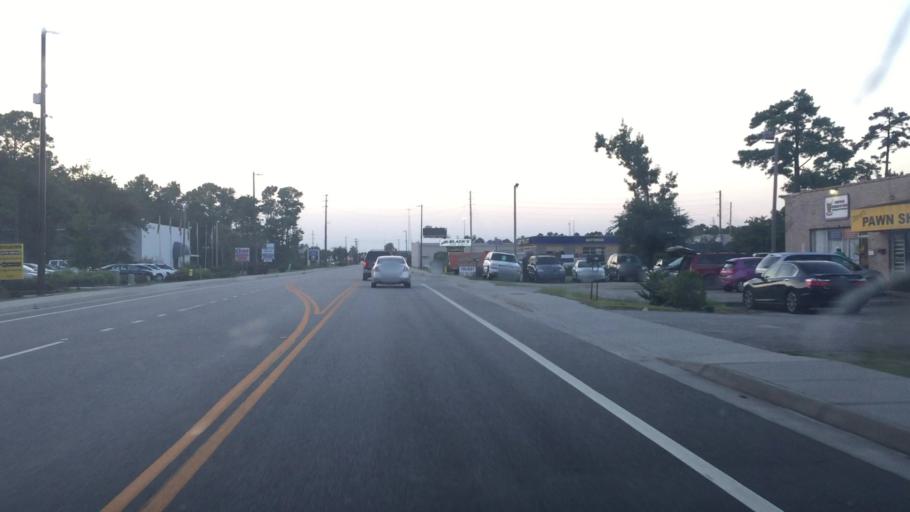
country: US
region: South Carolina
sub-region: Horry County
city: Myrtle Beach
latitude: 33.6948
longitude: -78.8977
